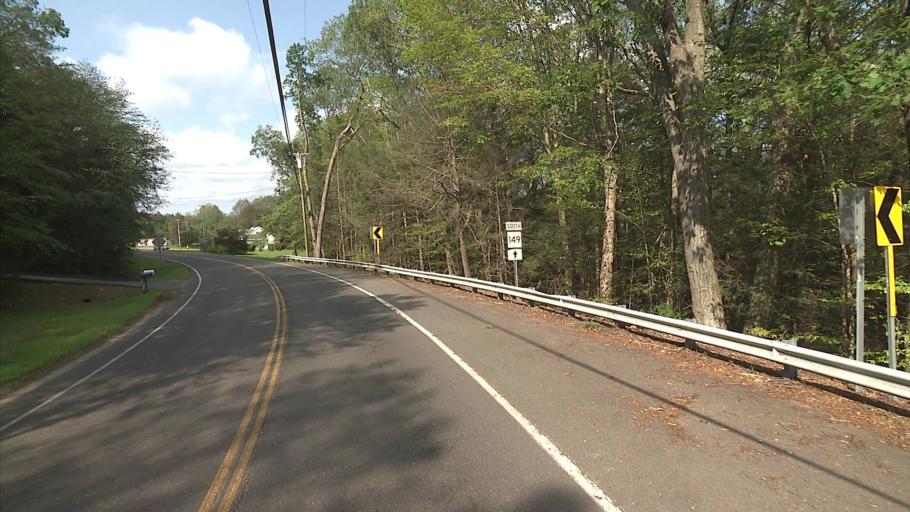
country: US
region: Connecticut
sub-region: Middlesex County
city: Moodus
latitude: 41.4965
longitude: -72.4575
